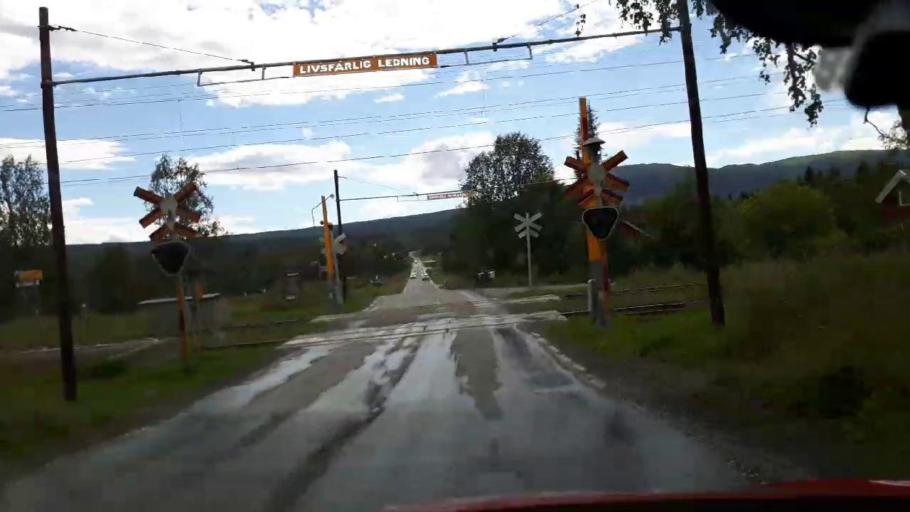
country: SE
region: Jaemtland
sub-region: Are Kommun
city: Are
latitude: 63.3159
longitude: 13.2358
